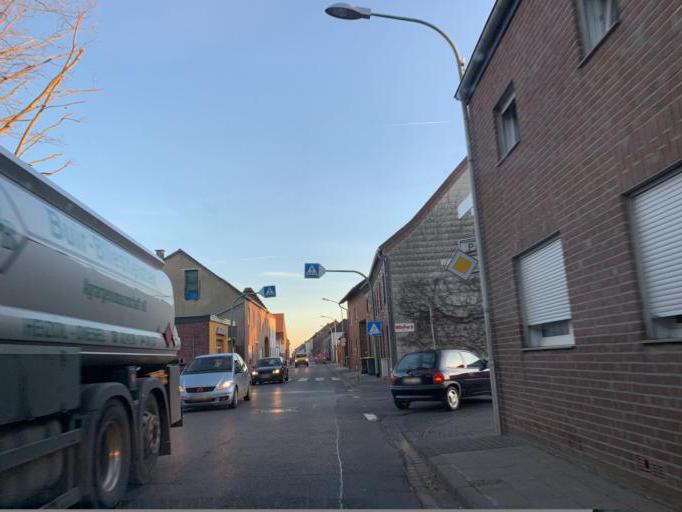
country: DE
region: North Rhine-Westphalia
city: Julich
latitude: 50.9607
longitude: 6.3789
